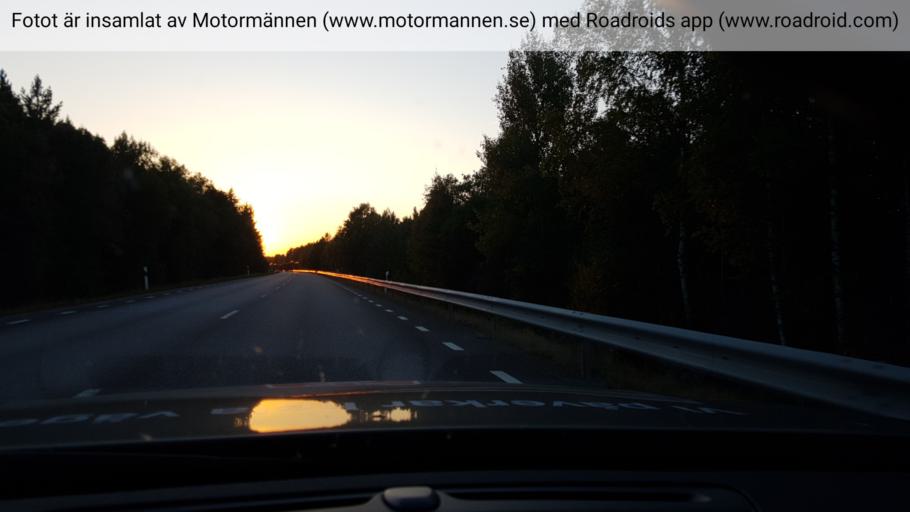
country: SE
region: Uppsala
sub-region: Osthammars Kommun
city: Bjorklinge
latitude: 59.9636
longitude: 17.3884
